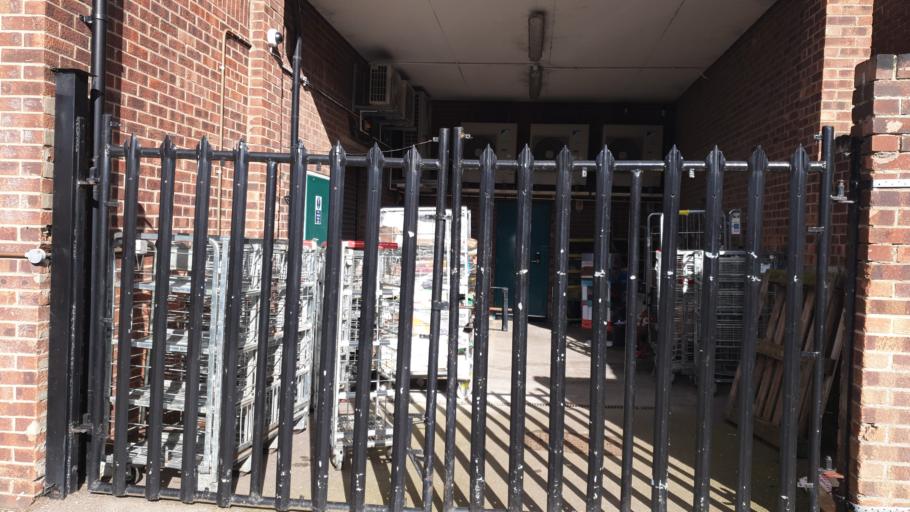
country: GB
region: England
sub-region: Essex
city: Brightlingsea
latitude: 51.8093
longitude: 1.0218
